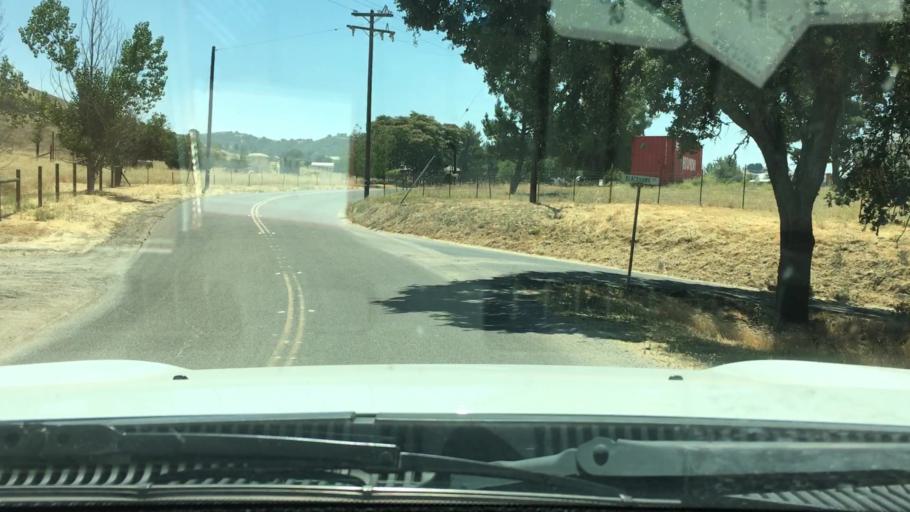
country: US
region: California
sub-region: San Luis Obispo County
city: Atascadero
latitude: 35.5194
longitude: -120.6407
